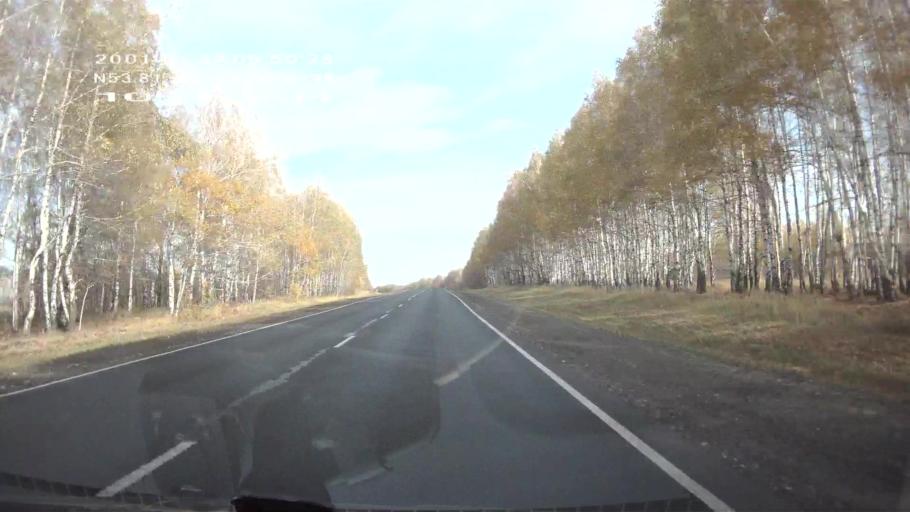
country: RU
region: Penza
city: Issa
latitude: 53.8158
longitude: 44.8386
